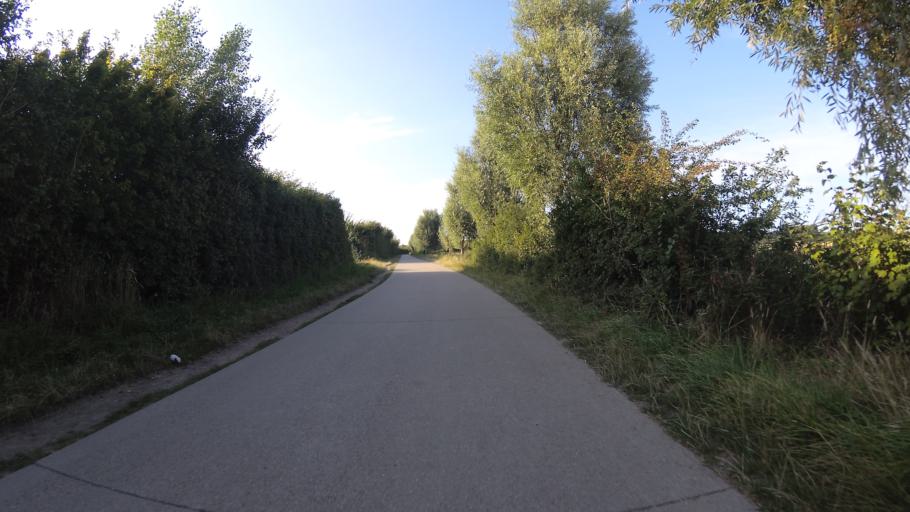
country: NL
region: Zeeland
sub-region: Gemeente Middelburg
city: Middelburg
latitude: 51.5639
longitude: 3.5239
